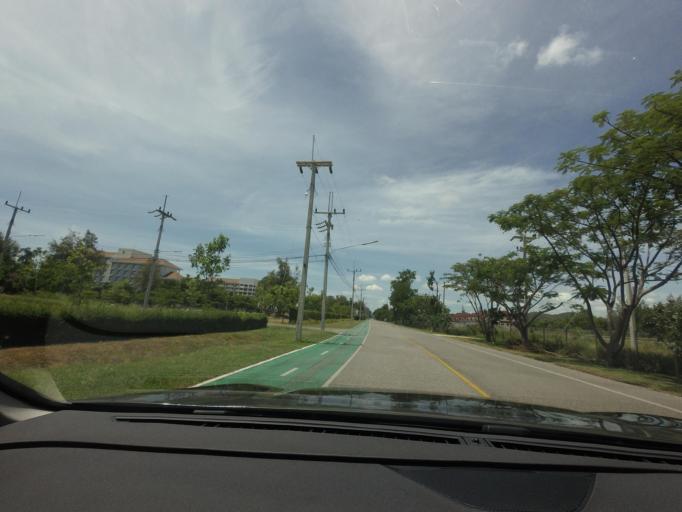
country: TH
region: Prachuap Khiri Khan
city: Hua Hin
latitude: 12.5045
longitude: 99.9727
